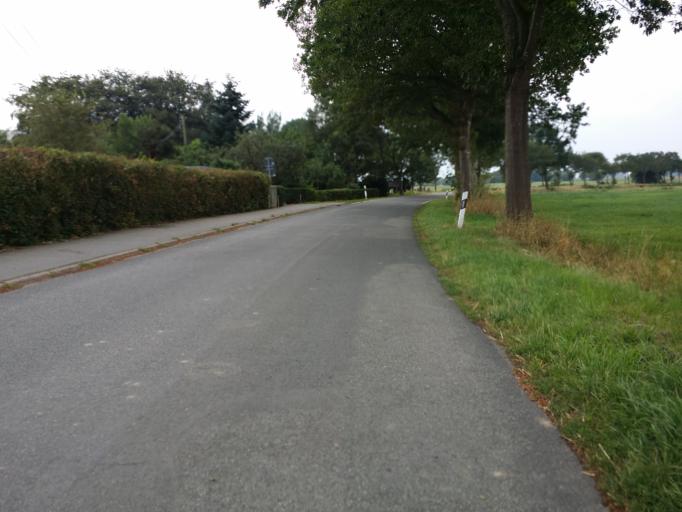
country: DE
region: Schleswig-Holstein
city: Heiligenstedtenerkamp
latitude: 53.8941
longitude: 9.4645
